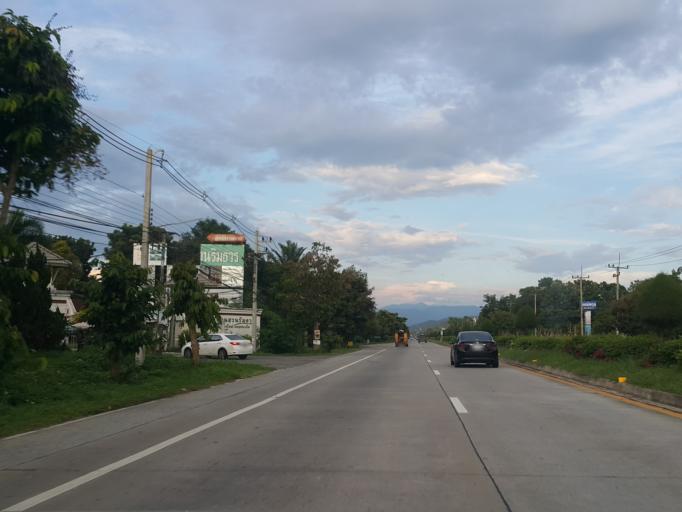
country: TH
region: Chiang Mai
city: San Sai
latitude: 18.8619
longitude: 99.1120
